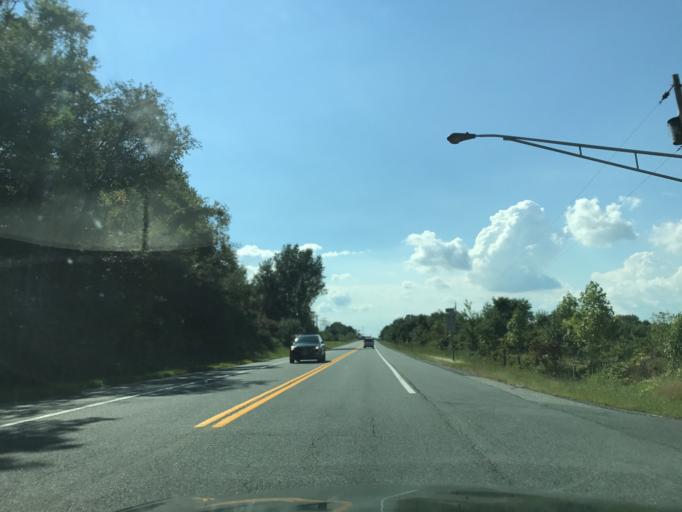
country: US
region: Maryland
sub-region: Harford County
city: Aberdeen
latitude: 39.5739
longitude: -76.1621
